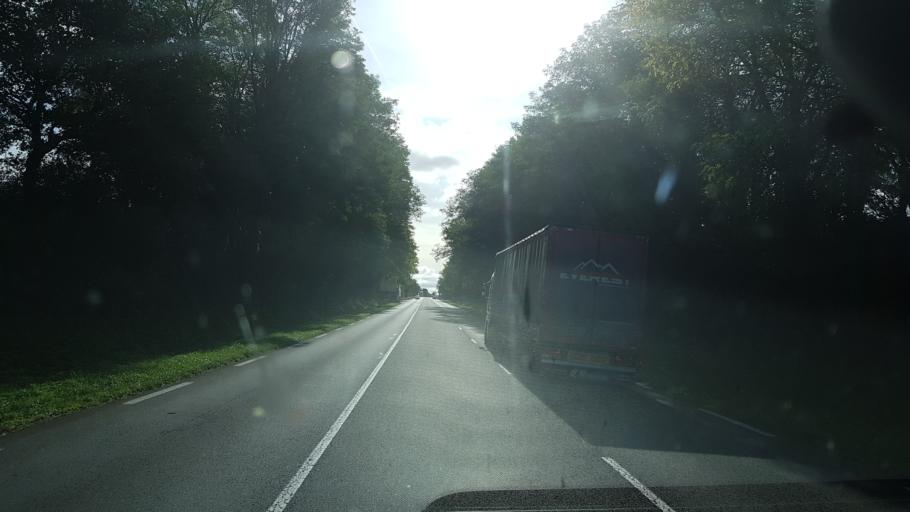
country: FR
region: Poitou-Charentes
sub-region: Departement de la Charente
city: Confolens
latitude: 46.0140
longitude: 0.6449
